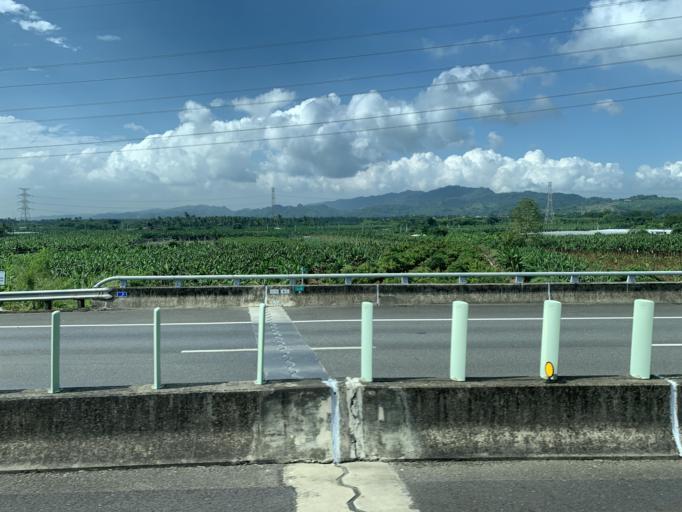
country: TW
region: Taiwan
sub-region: Pingtung
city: Pingtung
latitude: 22.8581
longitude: 120.4935
